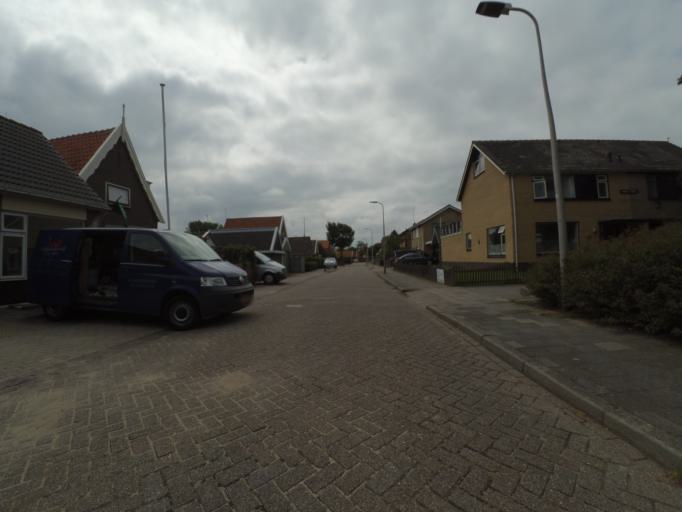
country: NL
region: North Holland
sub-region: Gemeente Texel
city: Den Burg
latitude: 53.0379
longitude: 4.8486
